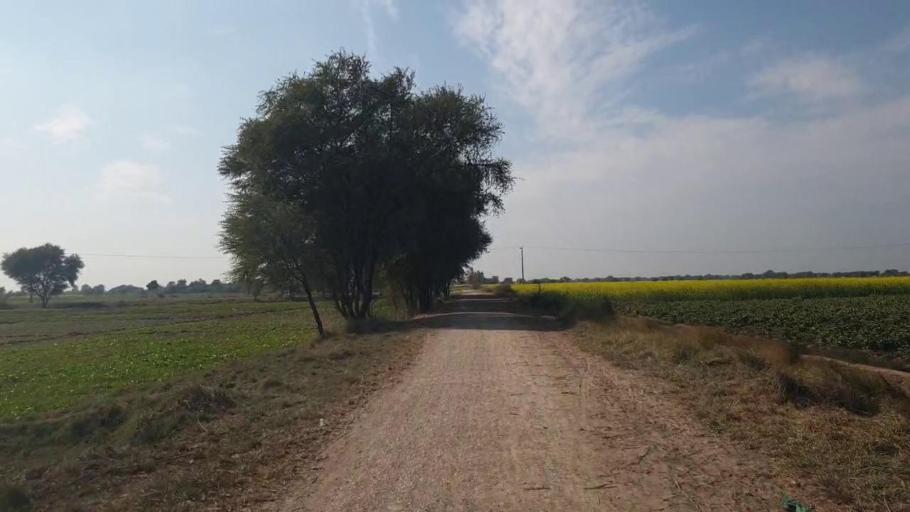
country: PK
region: Sindh
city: Shahdadpur
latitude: 25.9889
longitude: 68.5494
